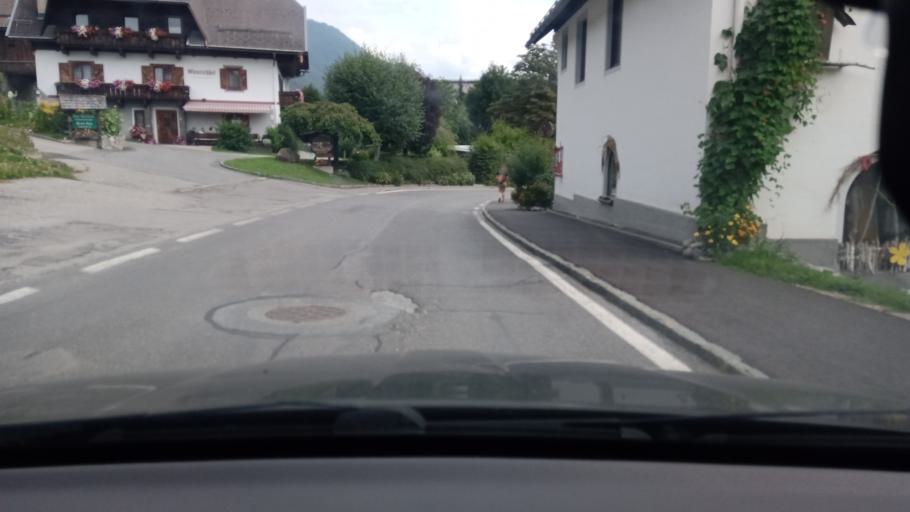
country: AT
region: Carinthia
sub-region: Politischer Bezirk Spittal an der Drau
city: Steinfeld
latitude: 46.7175
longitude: 13.2931
